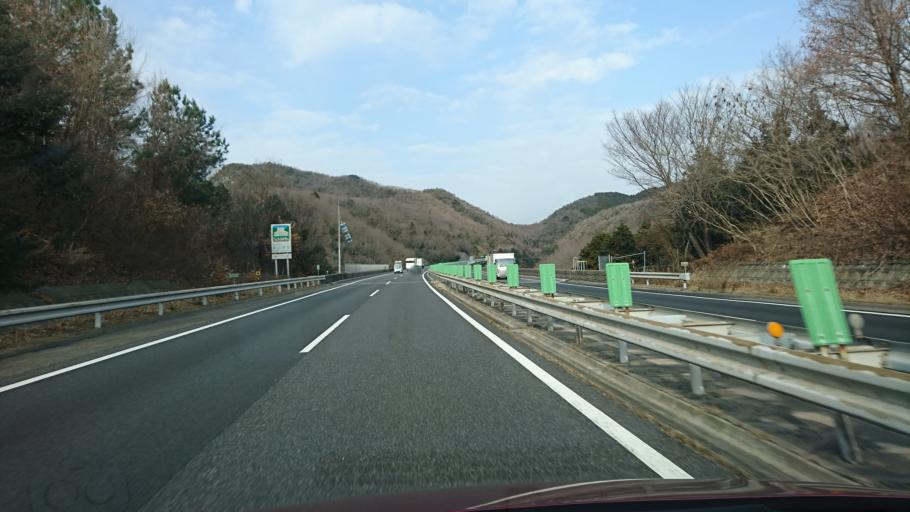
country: JP
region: Hyogo
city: Kariya
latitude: 34.7833
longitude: 134.2204
